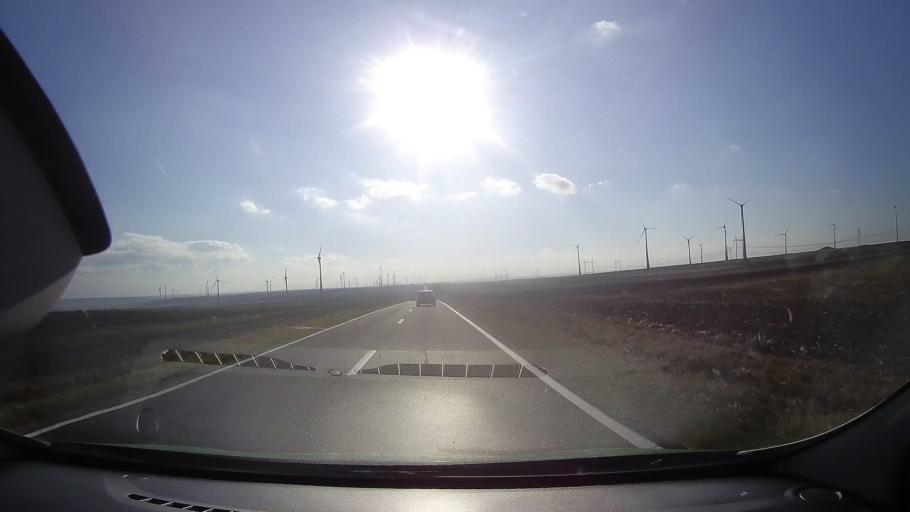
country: RO
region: Tulcea
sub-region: Comuna Topolog
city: Topolog
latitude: 44.8174
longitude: 28.2591
